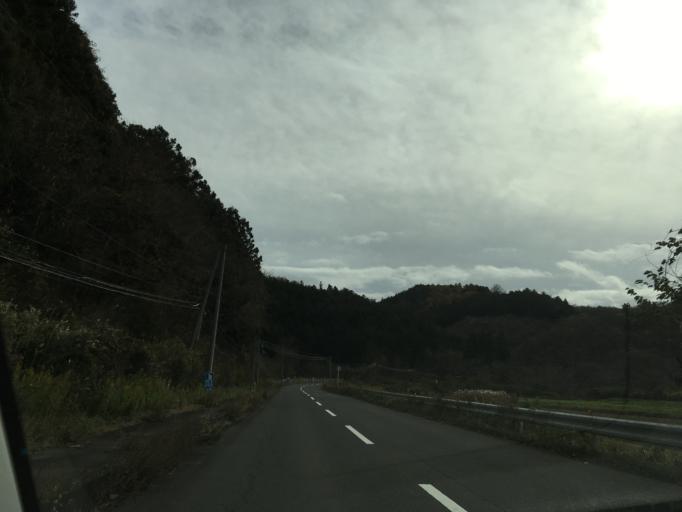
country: JP
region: Iwate
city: Ichinoseki
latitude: 38.7528
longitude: 141.2849
